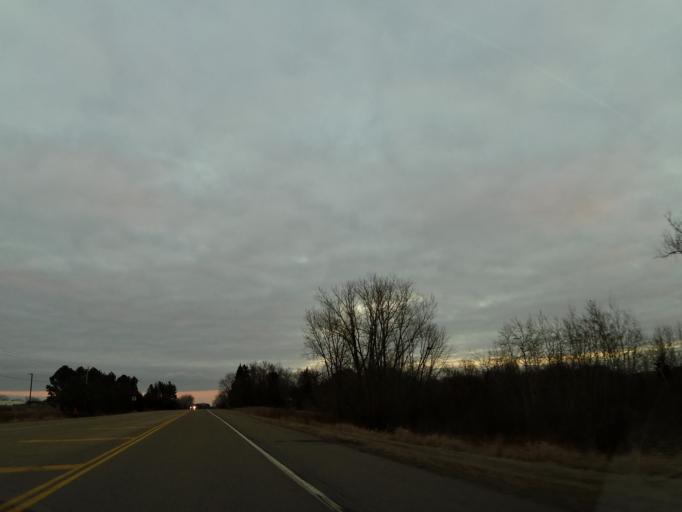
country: US
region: Minnesota
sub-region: Washington County
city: Mahtomedi
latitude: 45.0576
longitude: -92.9347
